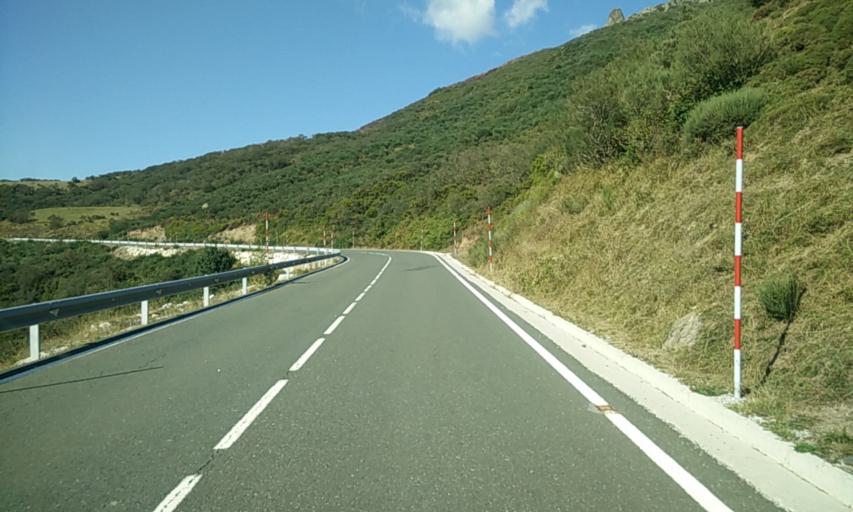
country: ES
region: Cantabria
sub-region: Provincia de Cantabria
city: Camaleno
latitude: 43.0756
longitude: -4.7372
